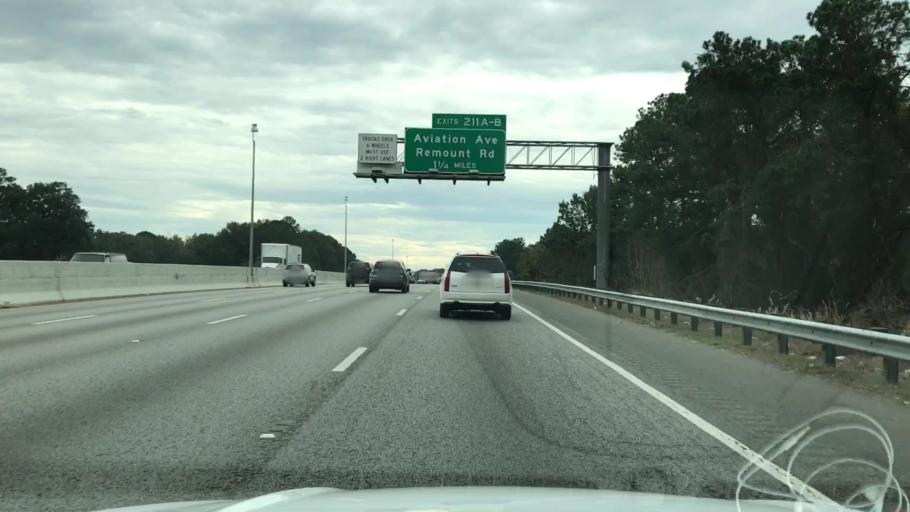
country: US
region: South Carolina
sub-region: Berkeley County
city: Hanahan
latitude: 32.9217
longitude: -80.0383
